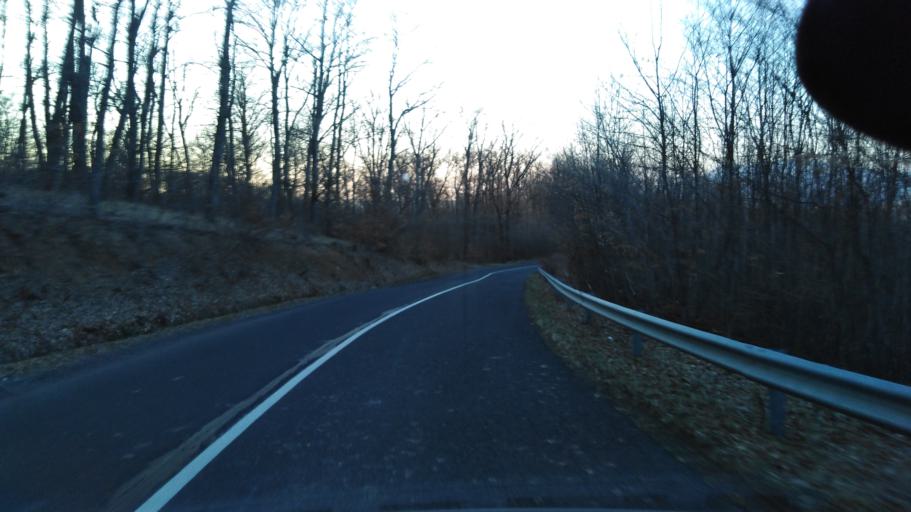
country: HU
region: Nograd
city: Salgotarjan
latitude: 48.0781
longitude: 19.8114
